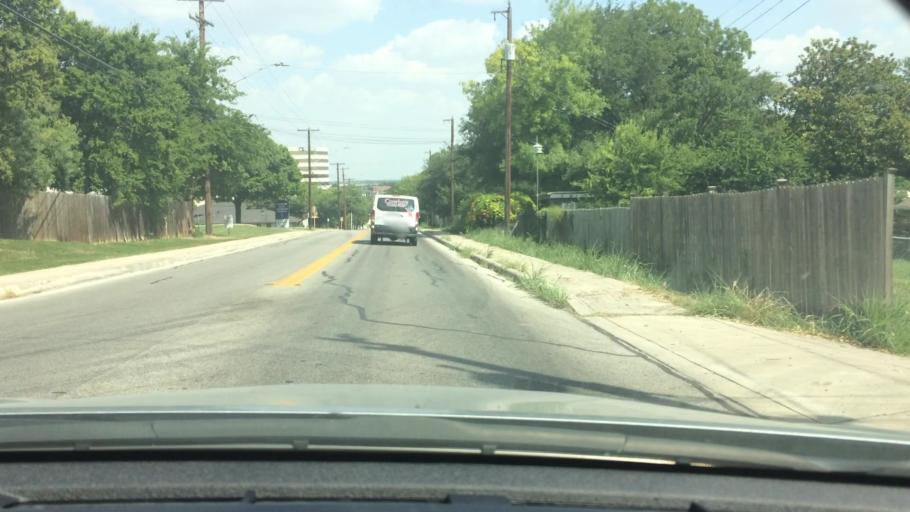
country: US
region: Texas
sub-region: Bexar County
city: Castle Hills
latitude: 29.5335
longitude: -98.4993
